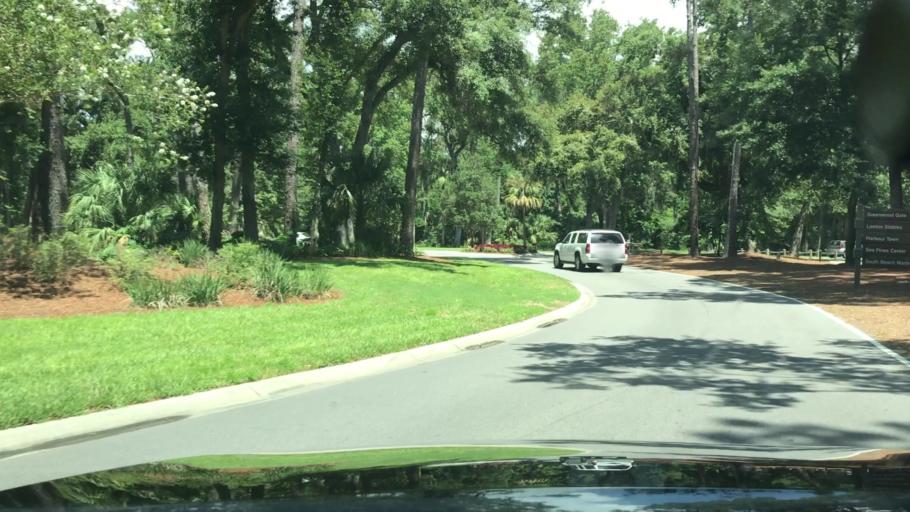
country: US
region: South Carolina
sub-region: Beaufort County
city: Hilton Head Island
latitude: 32.1314
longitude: -80.7956
